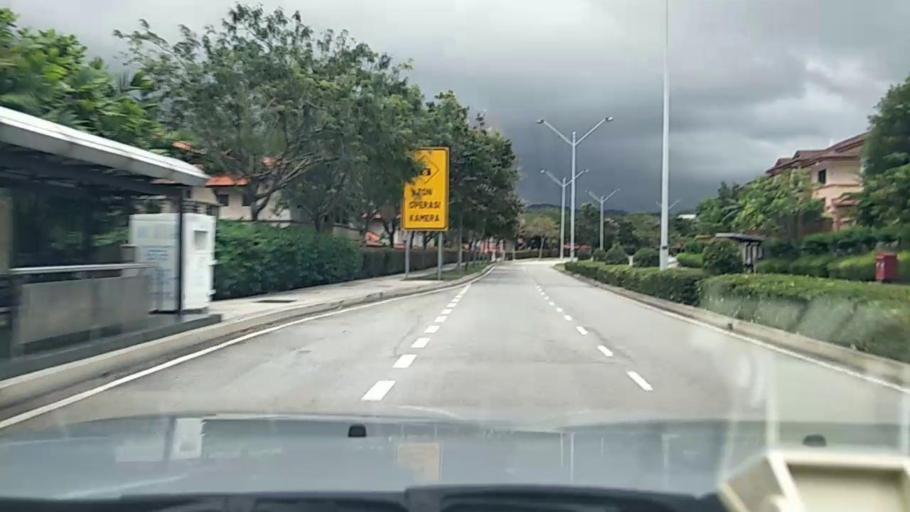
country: MY
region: Putrajaya
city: Putrajaya
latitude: 2.9325
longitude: 101.7034
